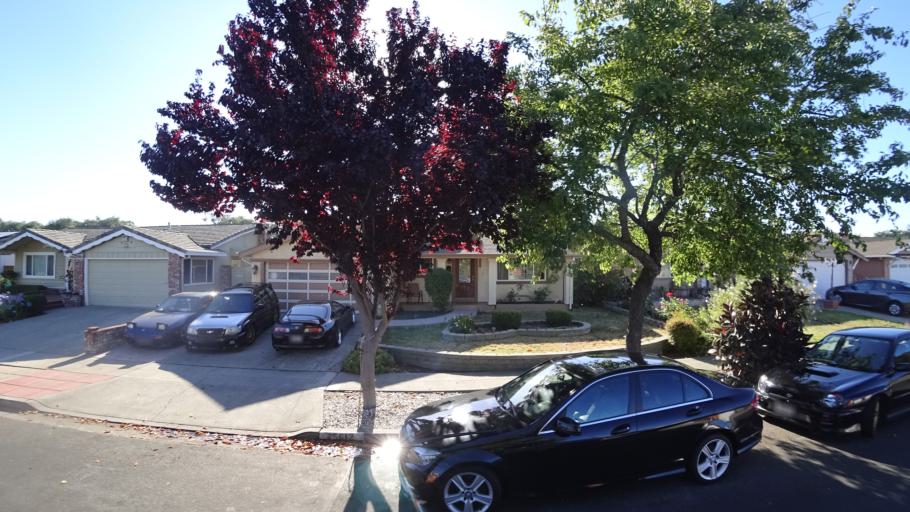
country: US
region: California
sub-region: Alameda County
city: Hayward
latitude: 37.6423
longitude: -122.0999
